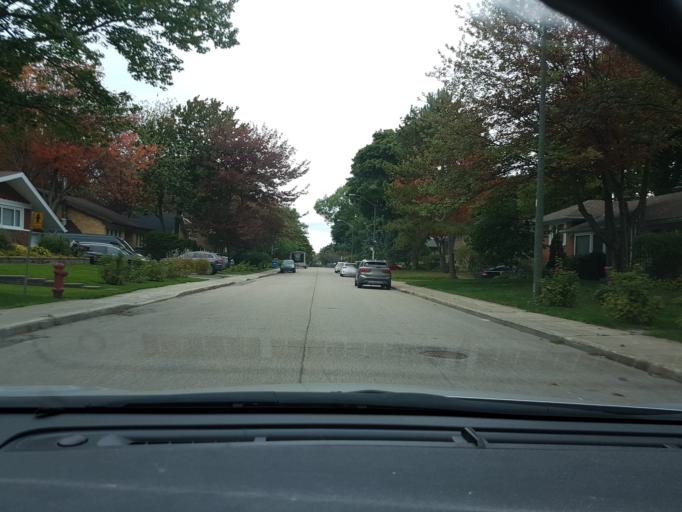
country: CA
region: Quebec
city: Quebec
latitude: 46.7860
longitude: -71.2617
